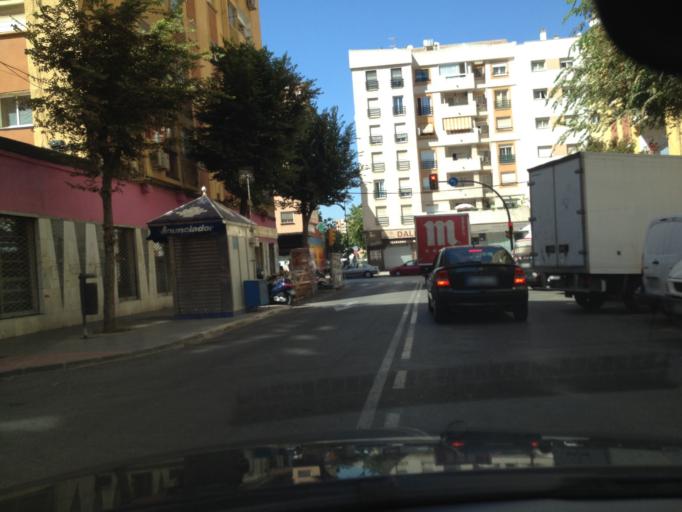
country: ES
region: Andalusia
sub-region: Provincia de Malaga
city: Malaga
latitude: 36.7056
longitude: -4.4374
